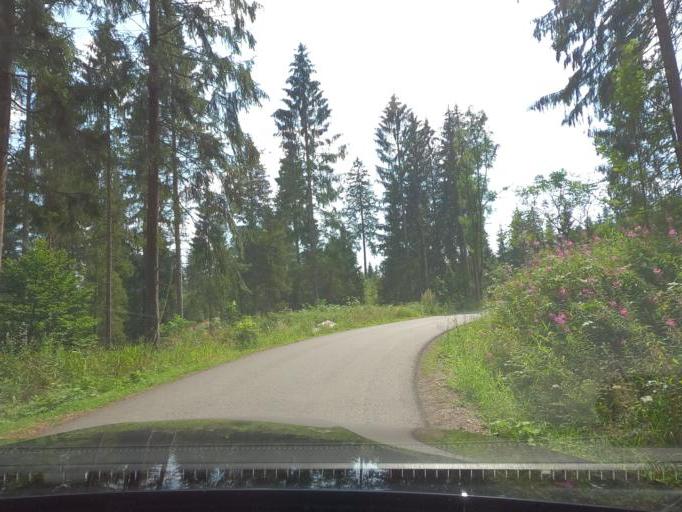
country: DE
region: Lower Saxony
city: Clausthal-Zellerfeld
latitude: 51.7749
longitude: 10.3067
